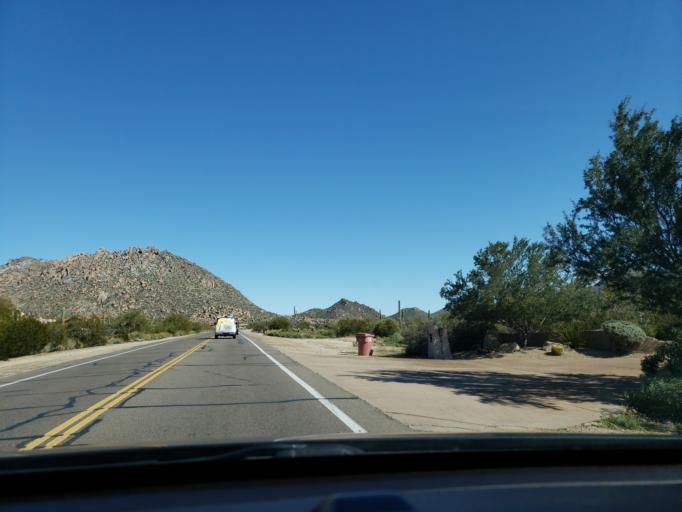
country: US
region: Arizona
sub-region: Maricopa County
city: Carefree
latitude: 33.7126
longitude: -111.8622
